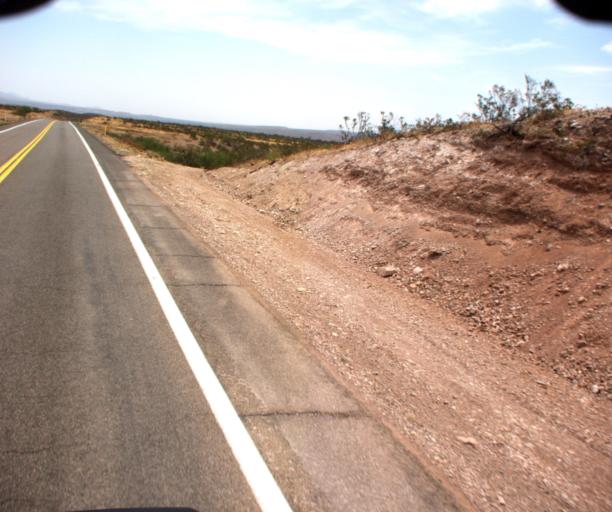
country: US
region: Arizona
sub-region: Graham County
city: Bylas
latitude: 33.2207
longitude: -110.2216
